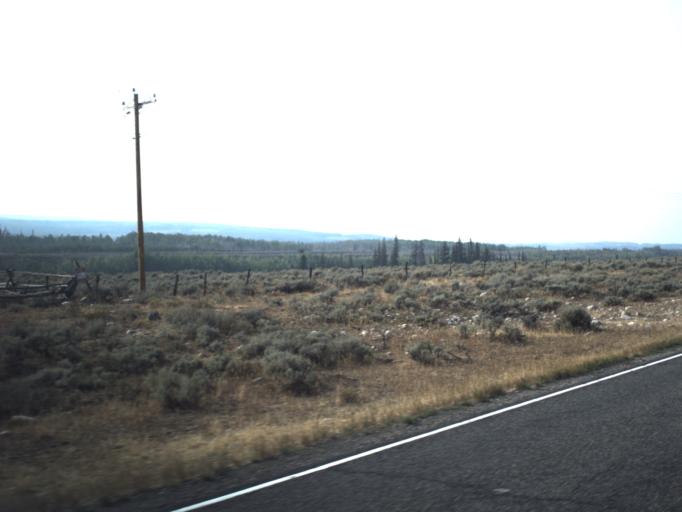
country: US
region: Wyoming
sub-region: Uinta County
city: Evanston
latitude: 40.9456
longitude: -110.8391
